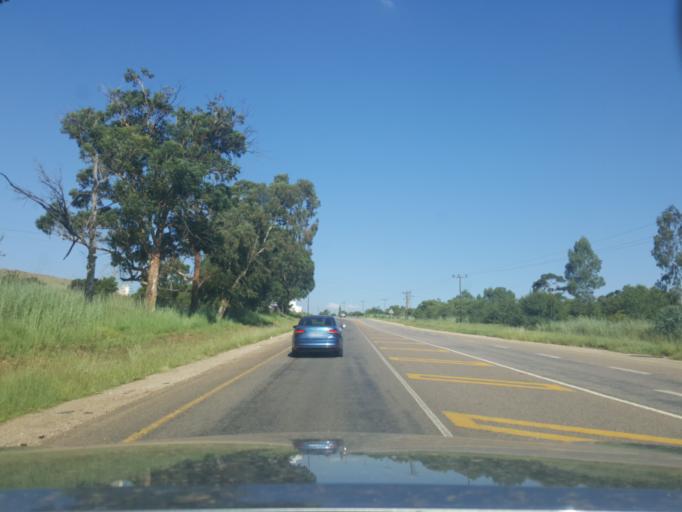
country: ZA
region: Gauteng
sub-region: City of Tshwane Metropolitan Municipality
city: Cullinan
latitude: -25.7731
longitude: 28.4525
